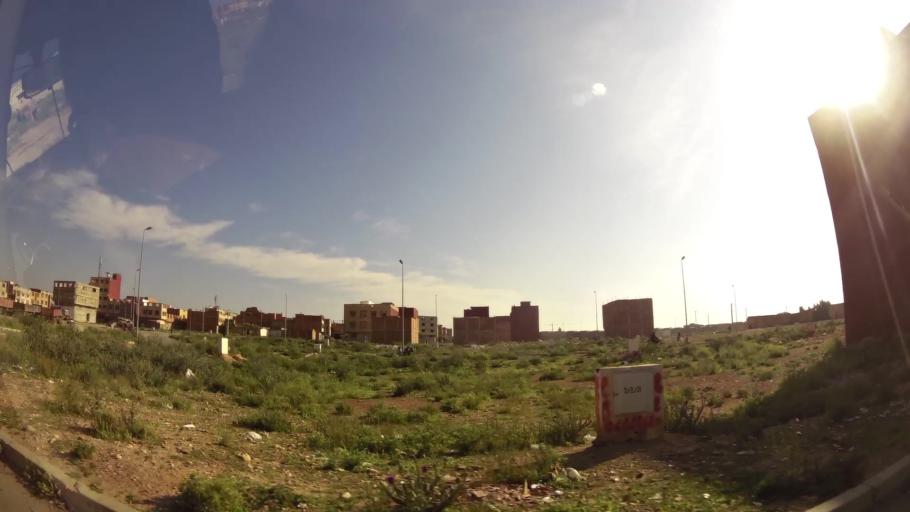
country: MA
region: Oriental
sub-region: Oujda-Angad
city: Oujda
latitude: 34.7175
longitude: -1.8933
